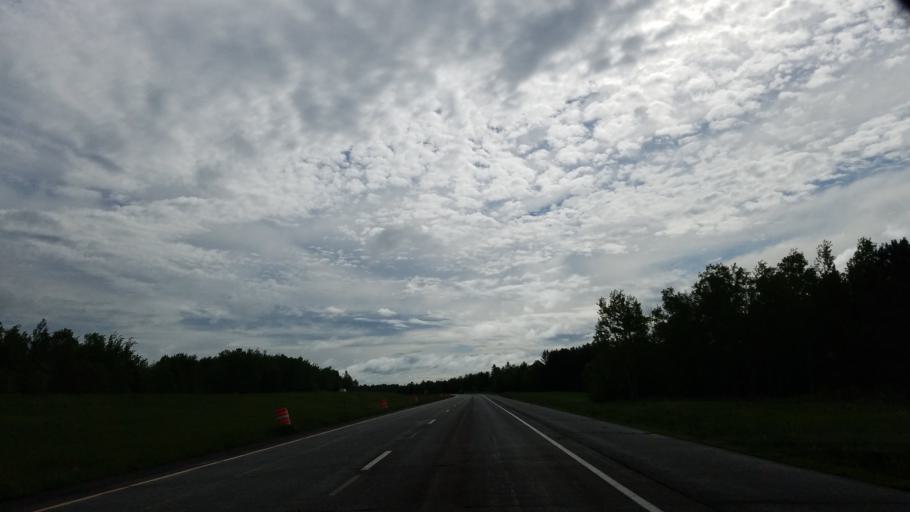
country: US
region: Minnesota
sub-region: Lake County
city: Two Harbors
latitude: 46.9299
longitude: -91.8357
